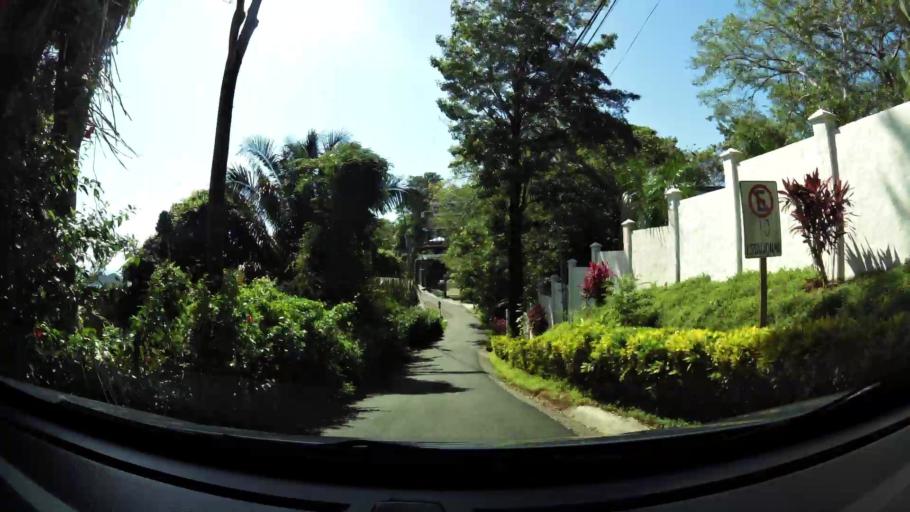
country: CR
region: Puntarenas
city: Quepos
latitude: 9.4019
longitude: -84.1618
